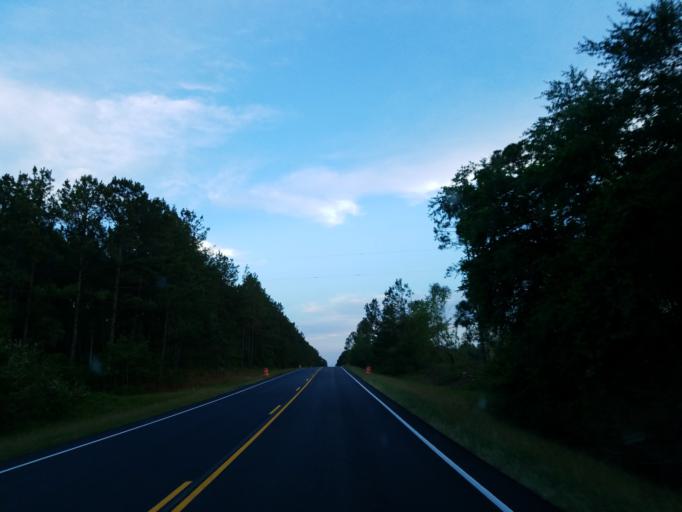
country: US
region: Georgia
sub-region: Turner County
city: Ashburn
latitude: 31.7278
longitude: -83.8082
